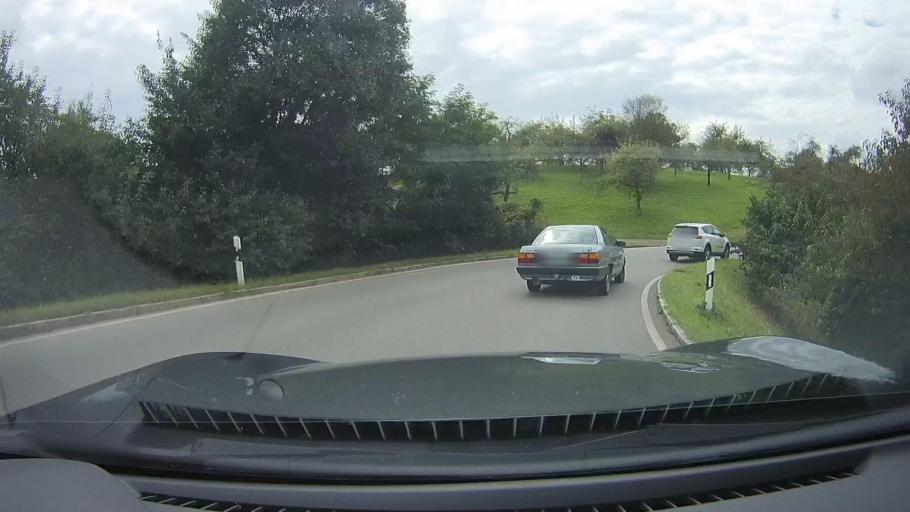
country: DE
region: Baden-Wuerttemberg
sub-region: Regierungsbezirk Stuttgart
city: Althutte
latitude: 48.8982
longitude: 9.5539
